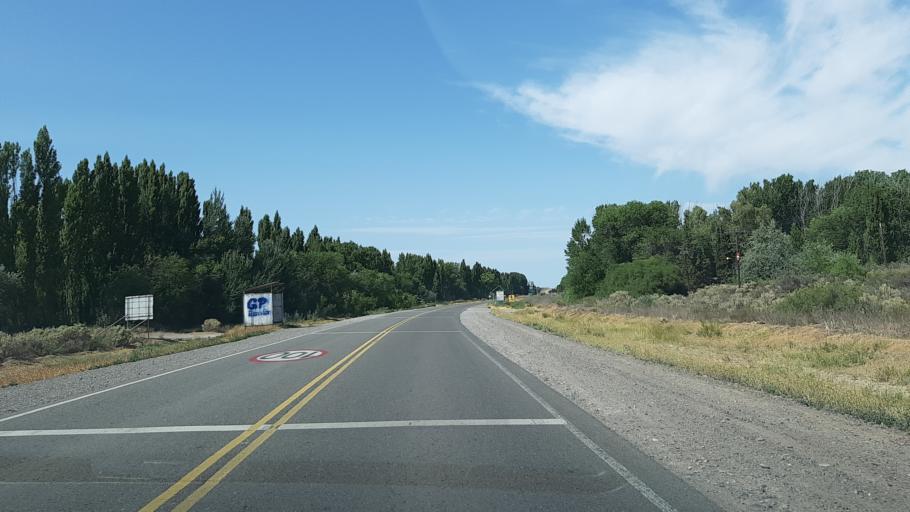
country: AR
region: Neuquen
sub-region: Departamento de Picun Leufu
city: Picun Leufu
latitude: -39.5275
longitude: -69.2977
